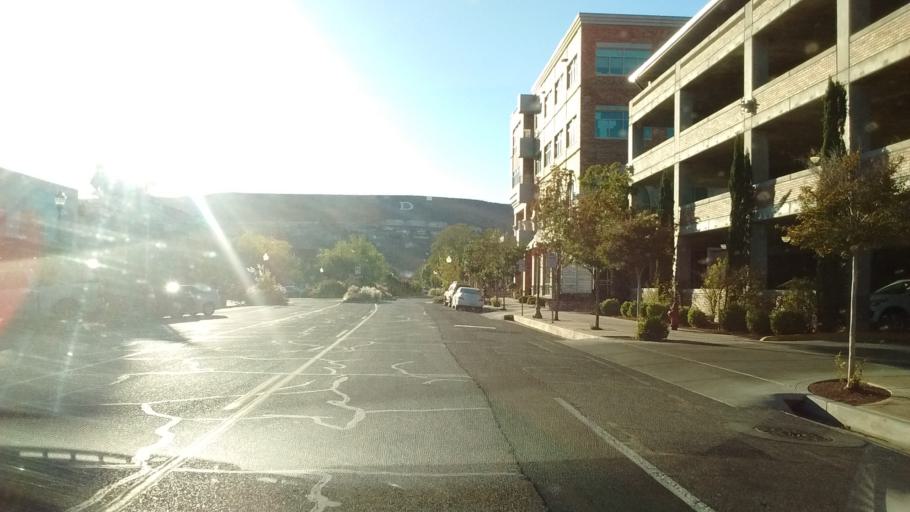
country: US
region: Utah
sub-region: Washington County
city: Saint George
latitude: 37.1083
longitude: -113.5822
